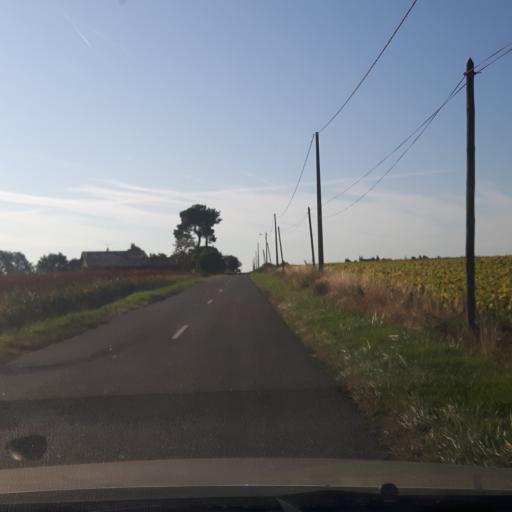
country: FR
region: Midi-Pyrenees
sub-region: Departement de la Haute-Garonne
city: Vacquiers
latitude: 43.7625
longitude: 1.4964
